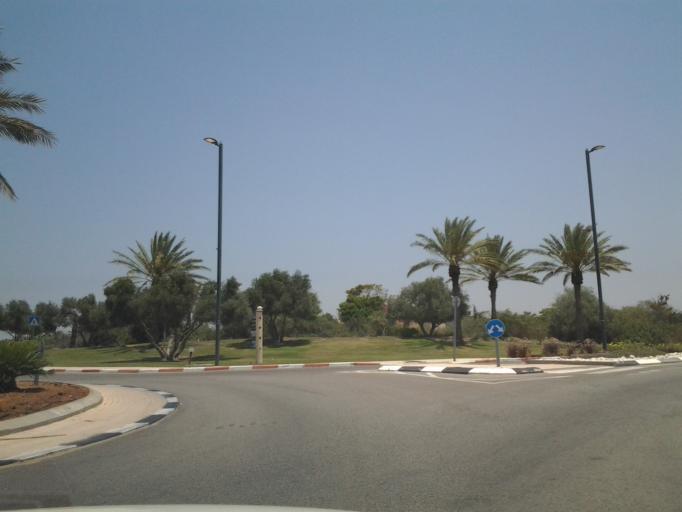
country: IL
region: Haifa
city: Qesarya
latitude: 32.4864
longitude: 34.9024
